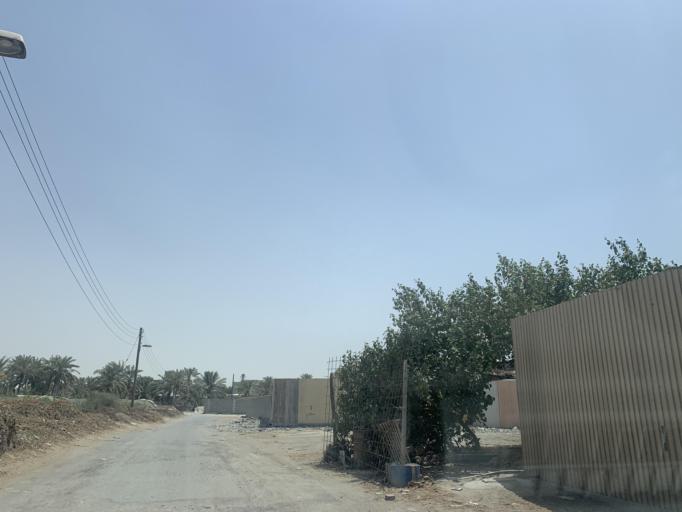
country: BH
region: Central Governorate
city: Madinat Hamad
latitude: 26.1549
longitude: 50.4965
